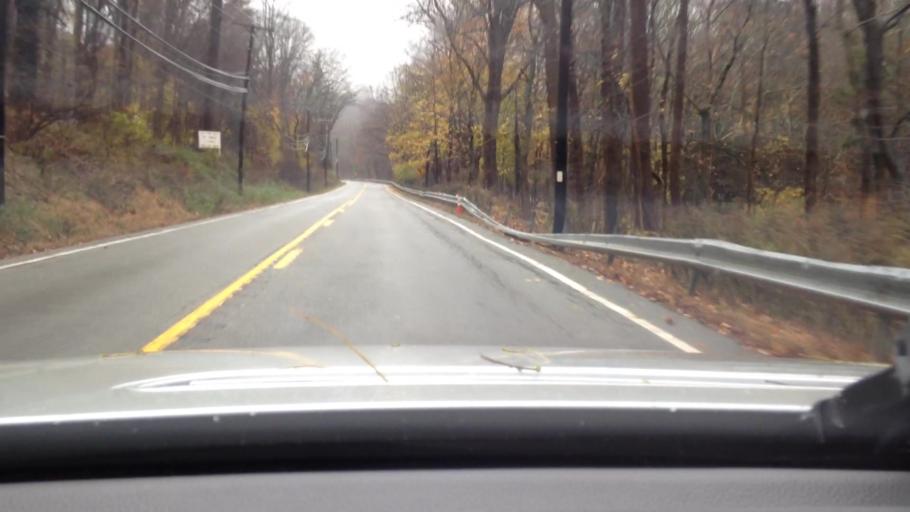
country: US
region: New York
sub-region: Orange County
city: West Point
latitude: 41.3663
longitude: -73.9285
